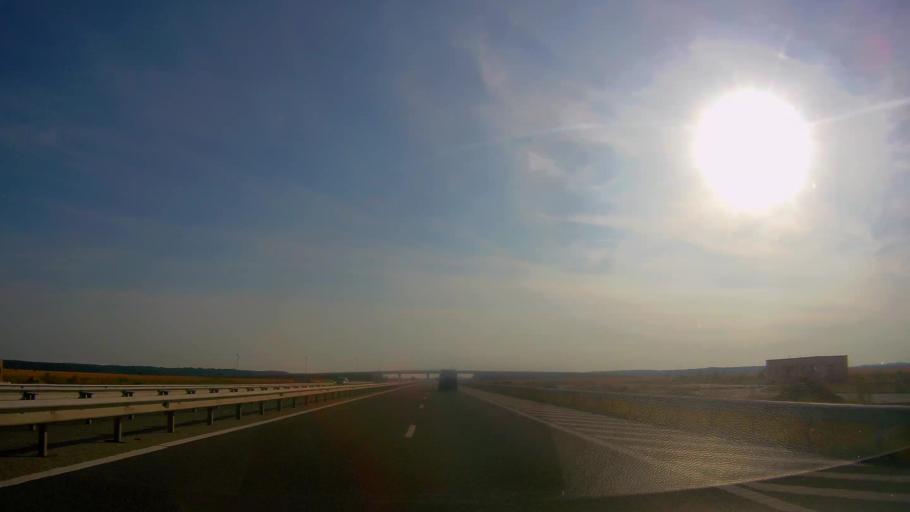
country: RO
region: Prahova
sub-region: Comuna Berceni
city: Corlatesti
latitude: 44.8867
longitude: 26.0923
